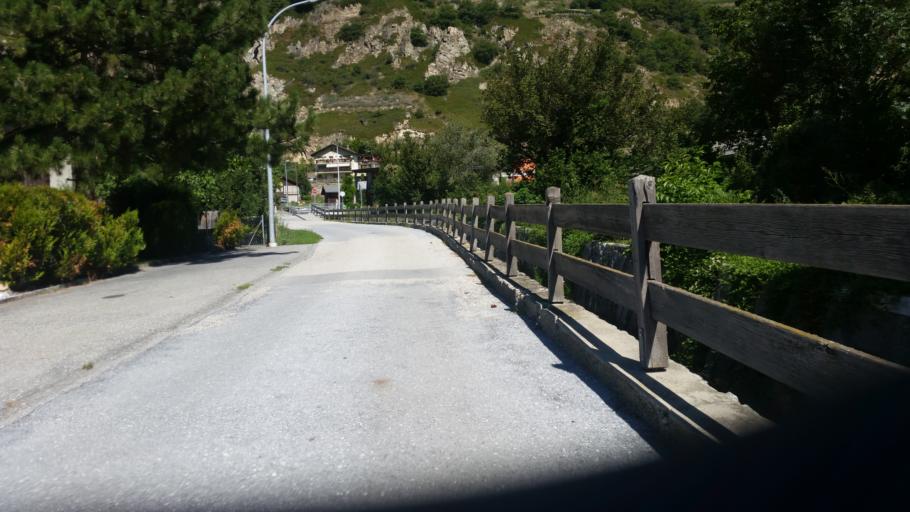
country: CH
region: Valais
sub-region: Leuk District
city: Turtmann
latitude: 46.3118
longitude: 7.7150
